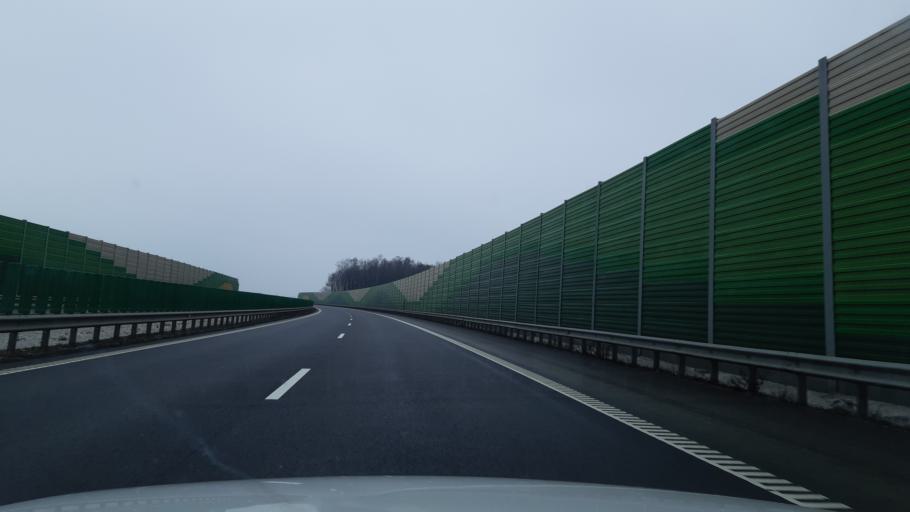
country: LT
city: Kazlu Ruda
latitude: 54.6703
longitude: 23.5224
